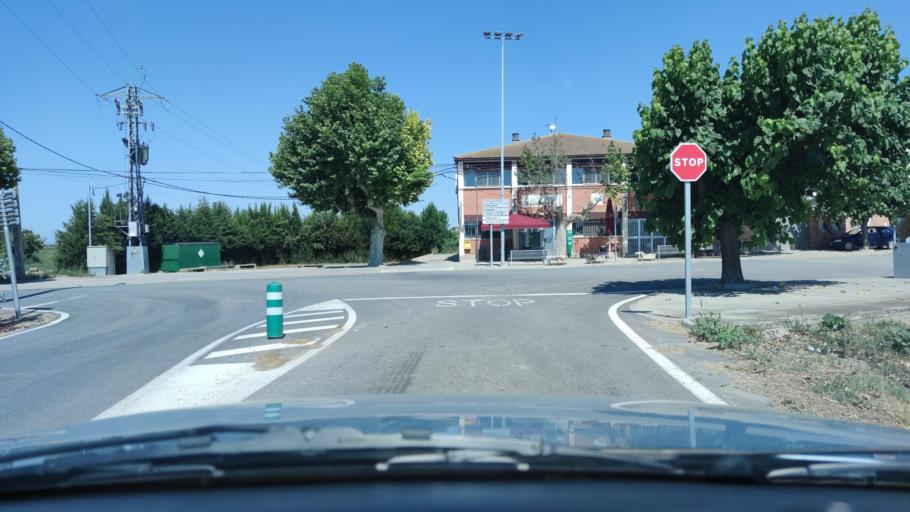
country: ES
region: Catalonia
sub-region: Provincia de Lleida
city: Linyola
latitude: 41.6959
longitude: 0.9511
